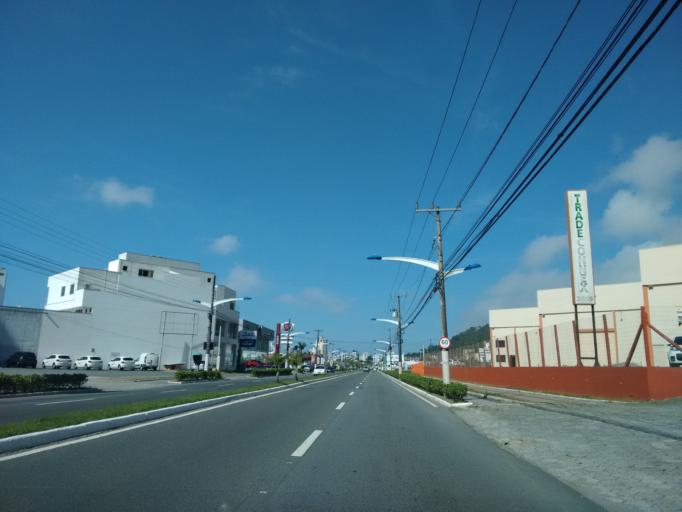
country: BR
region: Santa Catarina
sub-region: Itajai
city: Itajai
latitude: -26.9270
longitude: -48.6811
